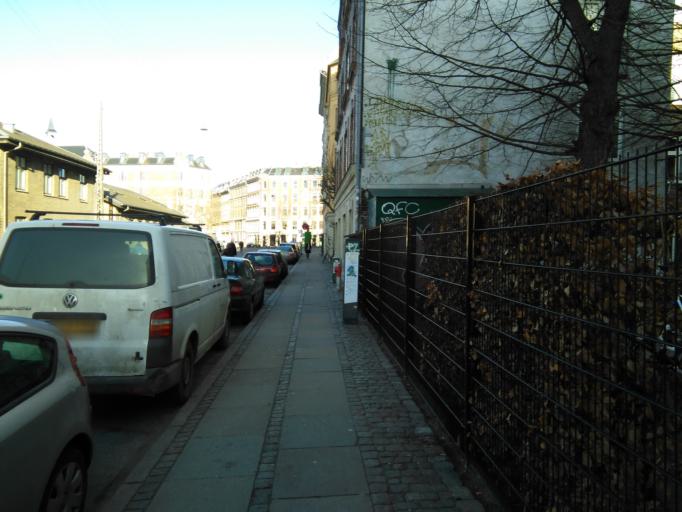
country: DK
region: Capital Region
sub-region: Kobenhavn
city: Copenhagen
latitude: 55.6702
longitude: 12.5627
